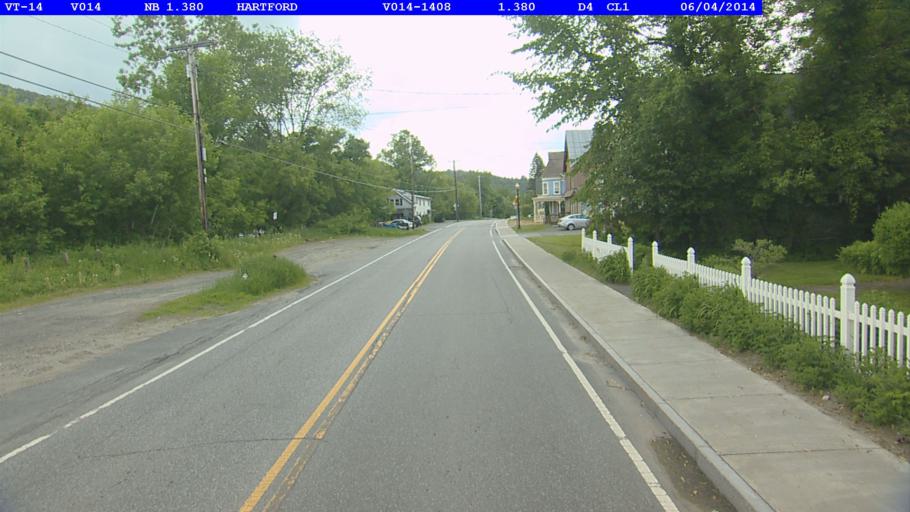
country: US
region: Vermont
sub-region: Windsor County
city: White River Junction
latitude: 43.6613
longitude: -72.3432
